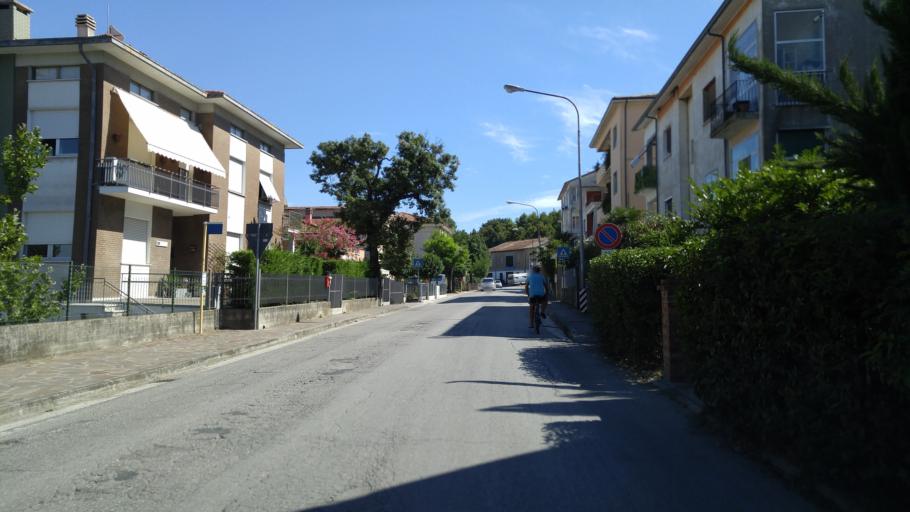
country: IT
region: The Marches
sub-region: Provincia di Pesaro e Urbino
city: Mondavio
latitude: 43.6825
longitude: 12.9587
